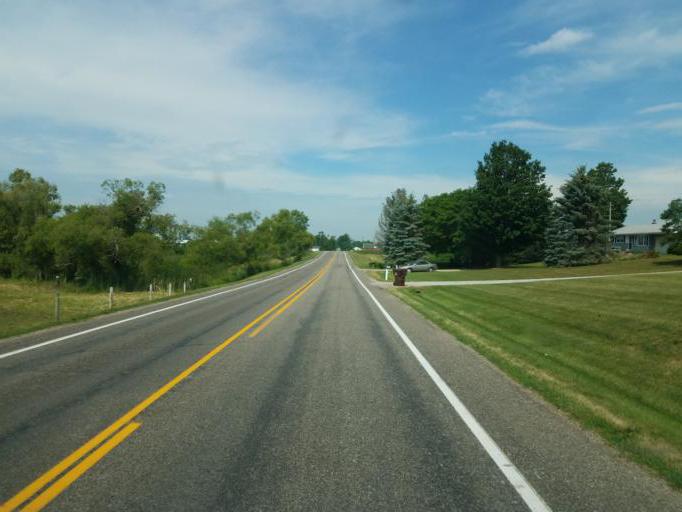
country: US
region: Michigan
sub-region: Eaton County
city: Charlotte
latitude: 42.6263
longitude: -84.9236
